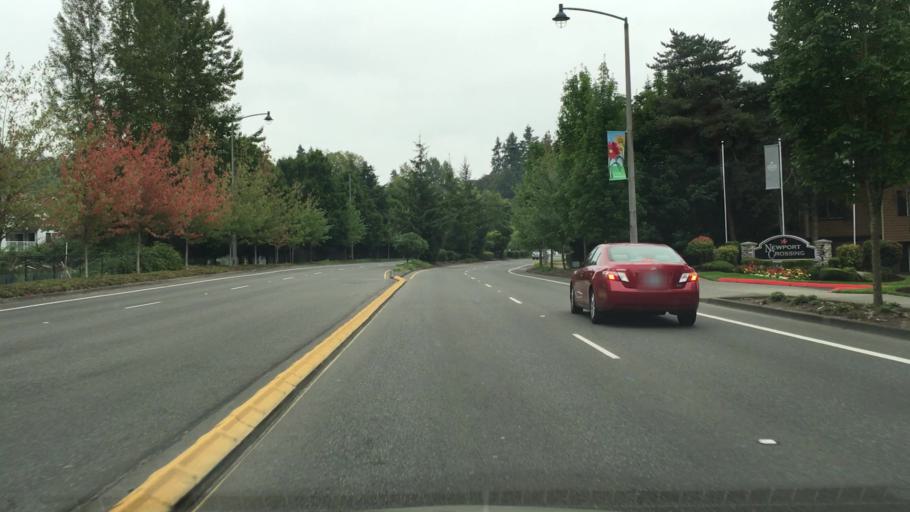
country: US
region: Washington
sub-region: King County
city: Newcastle
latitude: 47.5367
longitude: -122.1650
